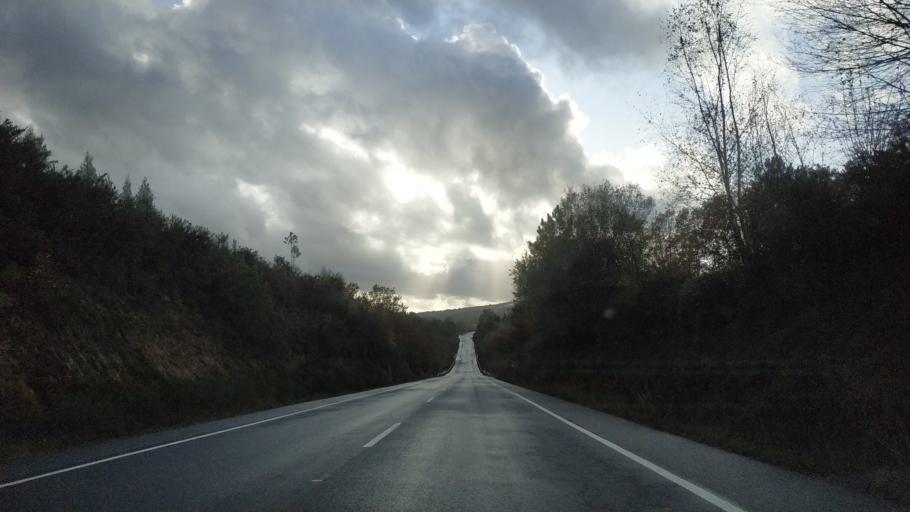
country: ES
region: Galicia
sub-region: Provincia da Coruna
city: Arzua
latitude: 42.9639
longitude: -8.1459
